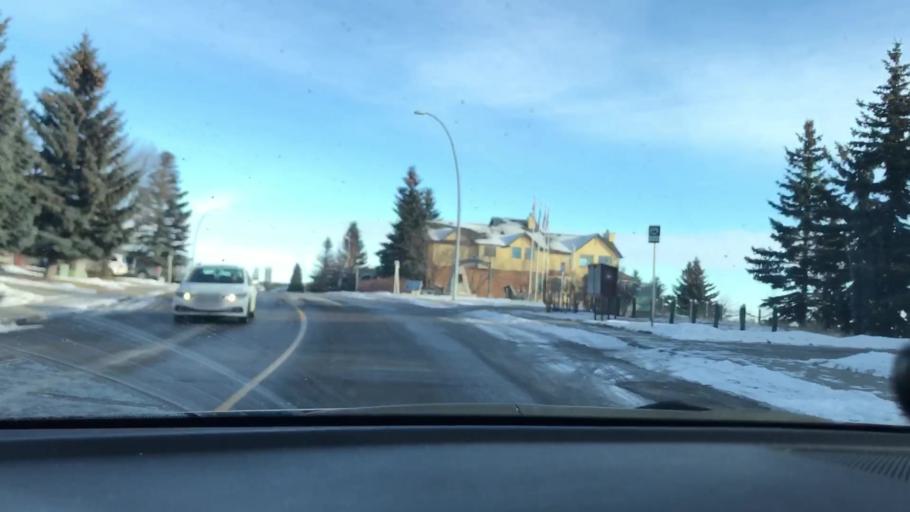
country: CA
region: Alberta
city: Calgary
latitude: 51.0215
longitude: -114.1748
